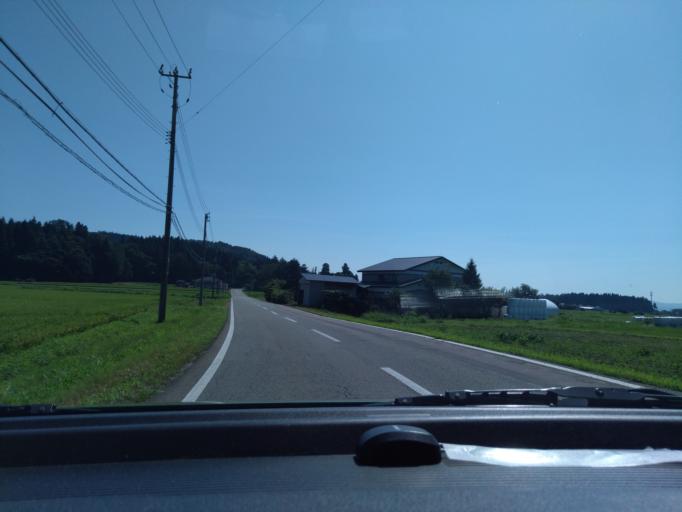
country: JP
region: Akita
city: Kakunodatemachi
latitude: 39.4744
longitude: 140.6086
